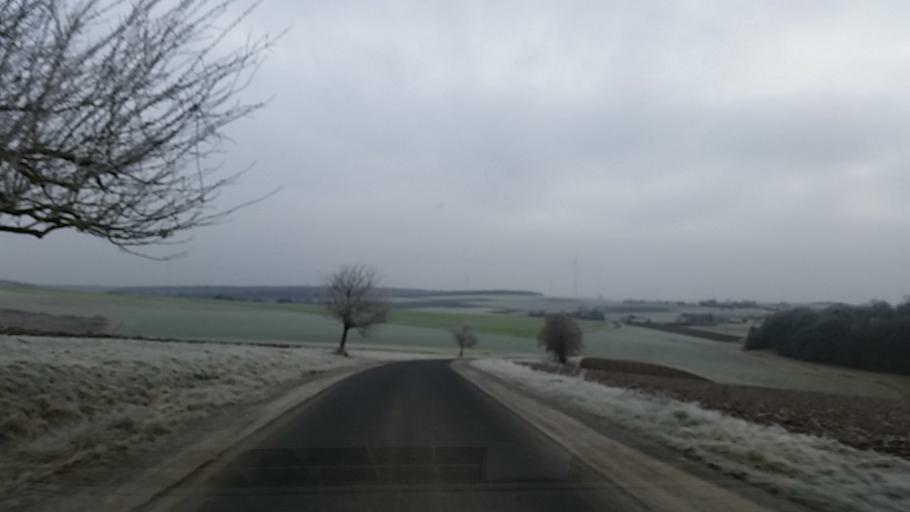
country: DE
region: Bavaria
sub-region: Regierungsbezirk Unterfranken
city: Fuchsstadt
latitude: 50.0433
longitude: 9.9122
